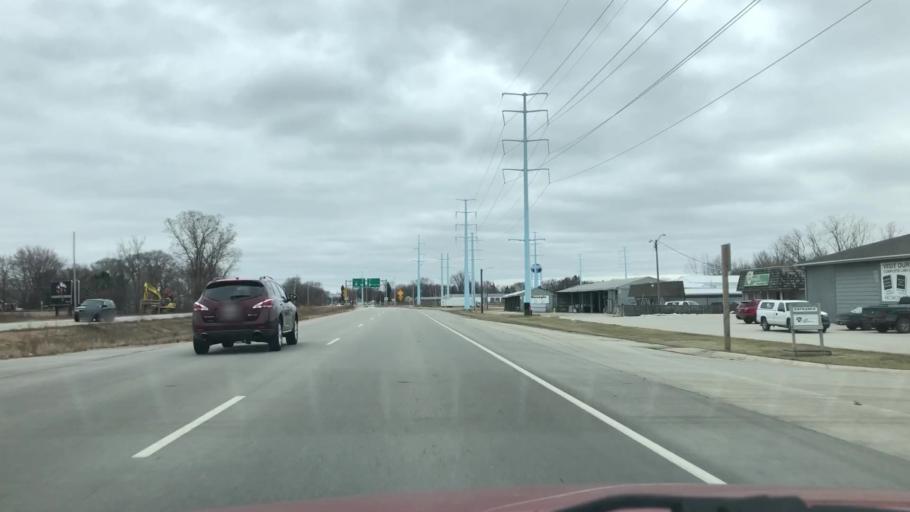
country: US
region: Wisconsin
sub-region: Brown County
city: De Pere
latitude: 44.4597
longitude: -88.0744
